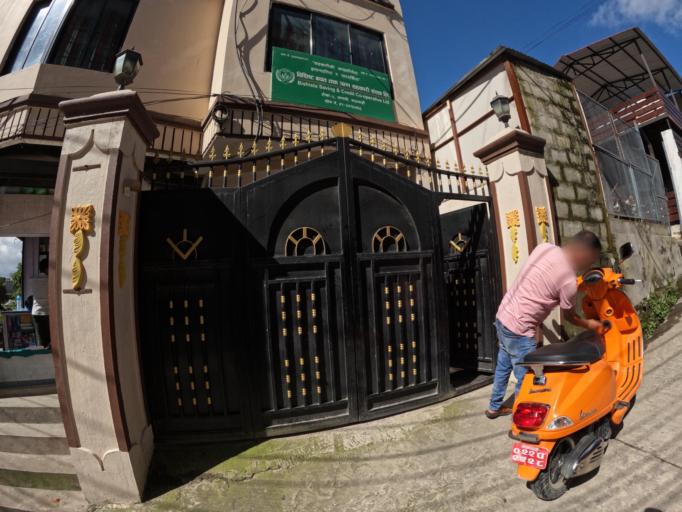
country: NP
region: Central Region
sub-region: Bagmati Zone
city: Kathmandu
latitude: 27.7461
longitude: 85.3347
